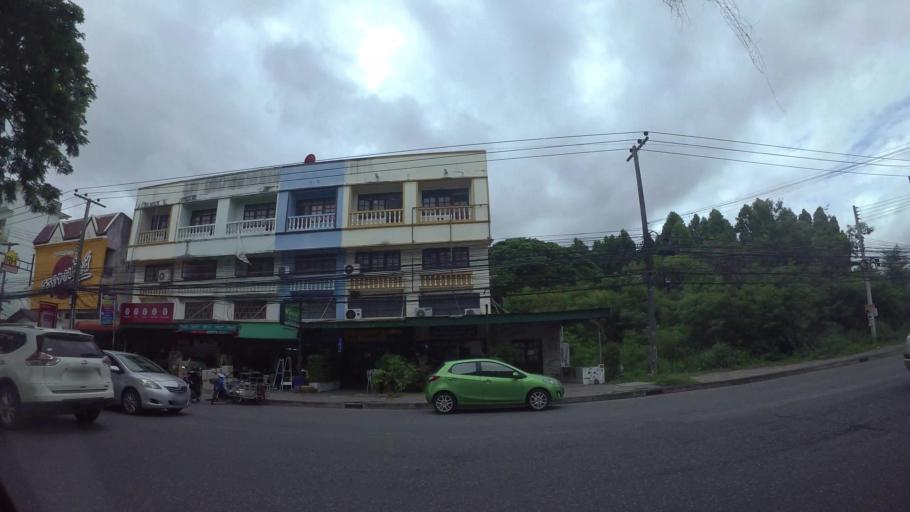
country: TH
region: Rayong
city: Rayong
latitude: 12.6704
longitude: 101.2752
